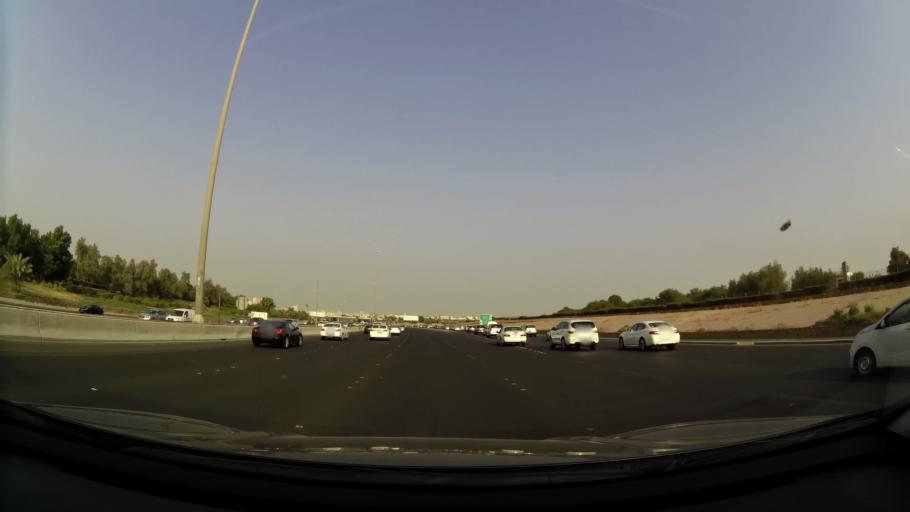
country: KW
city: Bayan
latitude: 29.3111
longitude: 48.0463
